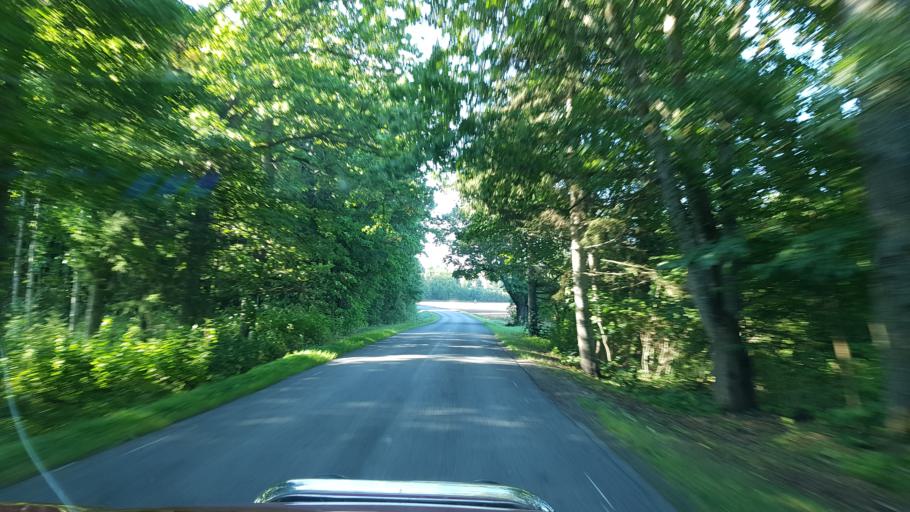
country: EE
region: Jogevamaa
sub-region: Jogeva linn
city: Jogeva
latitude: 58.7281
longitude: 26.5174
